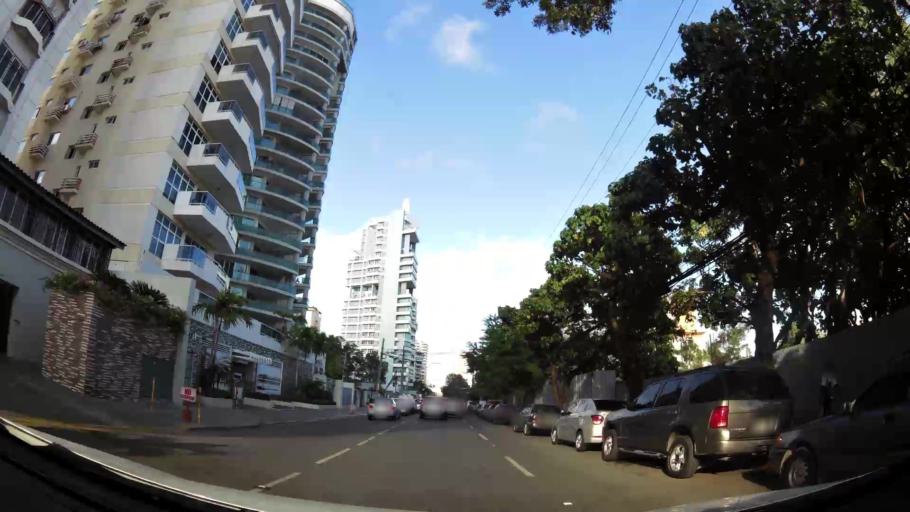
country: DO
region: Nacional
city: La Julia
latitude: 18.4668
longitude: -69.9225
